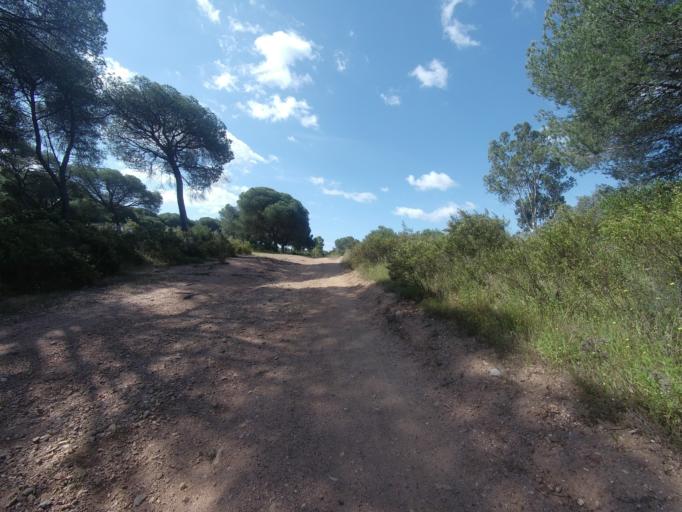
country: ES
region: Andalusia
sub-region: Provincia de Huelva
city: Aljaraque
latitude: 37.2366
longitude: -7.0305
